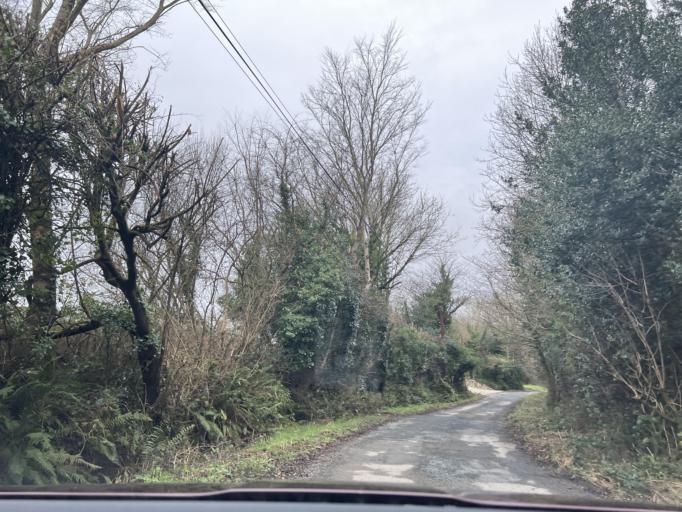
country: IE
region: Leinster
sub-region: Loch Garman
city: Castlebridge
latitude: 52.3854
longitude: -6.5527
